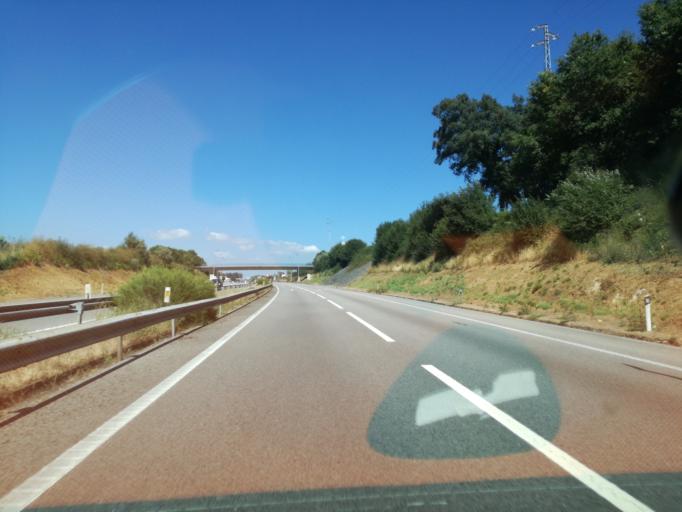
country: PT
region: Braga
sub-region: Vila Nova de Famalicao
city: Vila Nova de Famalicao
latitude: 41.3866
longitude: -8.4847
